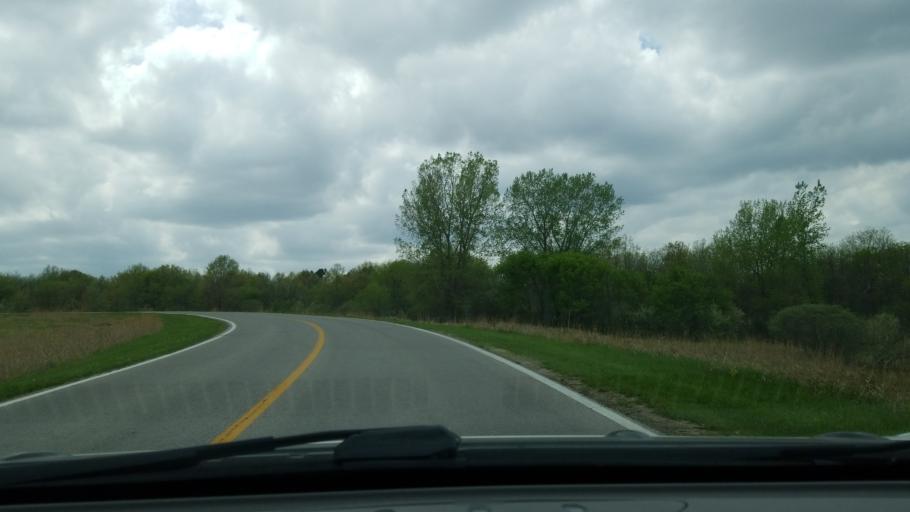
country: US
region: Nebraska
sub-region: Sarpy County
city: Chalco
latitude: 41.1699
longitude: -96.1659
